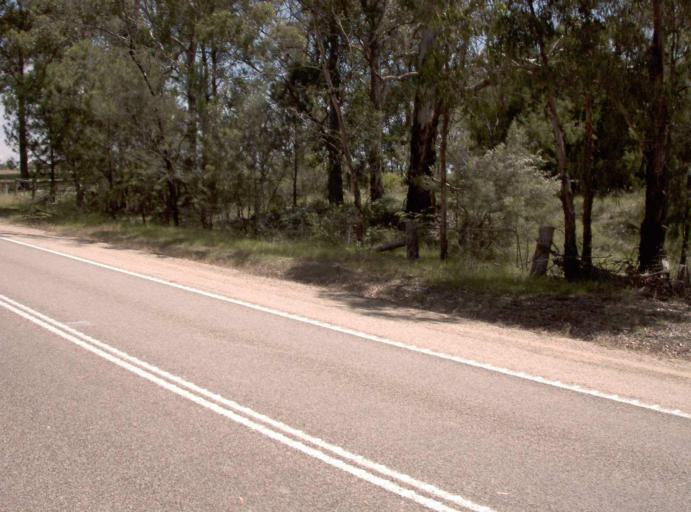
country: AU
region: Victoria
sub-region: East Gippsland
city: Bairnsdale
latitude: -37.7747
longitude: 147.6884
